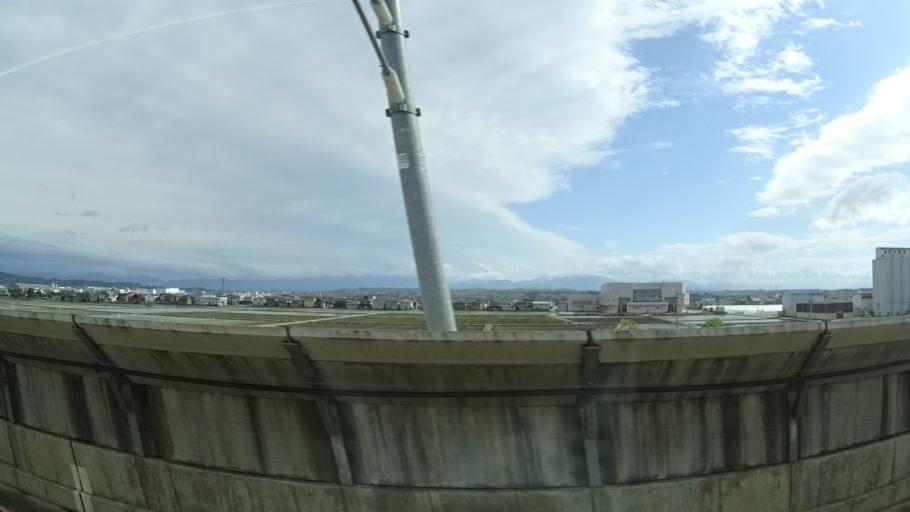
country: JP
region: Toyama
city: Kuragaki-kosugi
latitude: 36.7270
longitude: 137.1137
